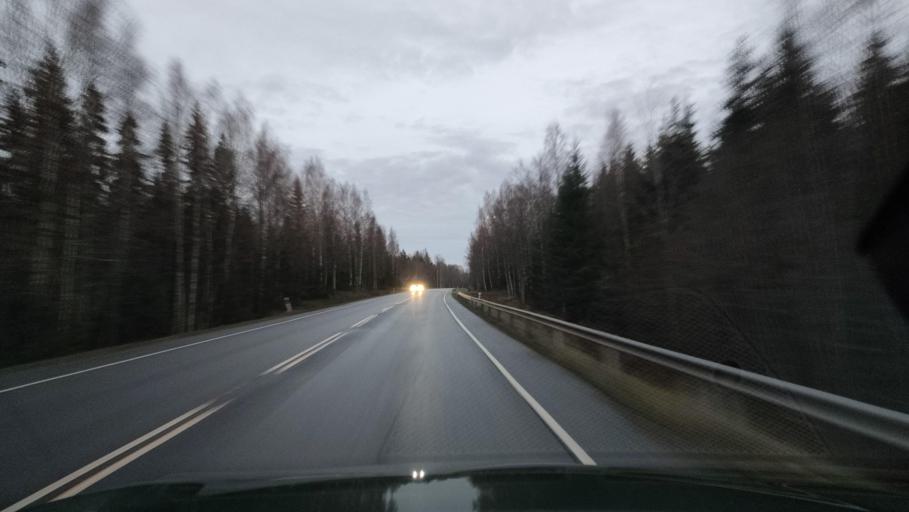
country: FI
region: Ostrobothnia
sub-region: Vaasa
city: Ristinummi
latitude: 62.9800
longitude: 21.7691
